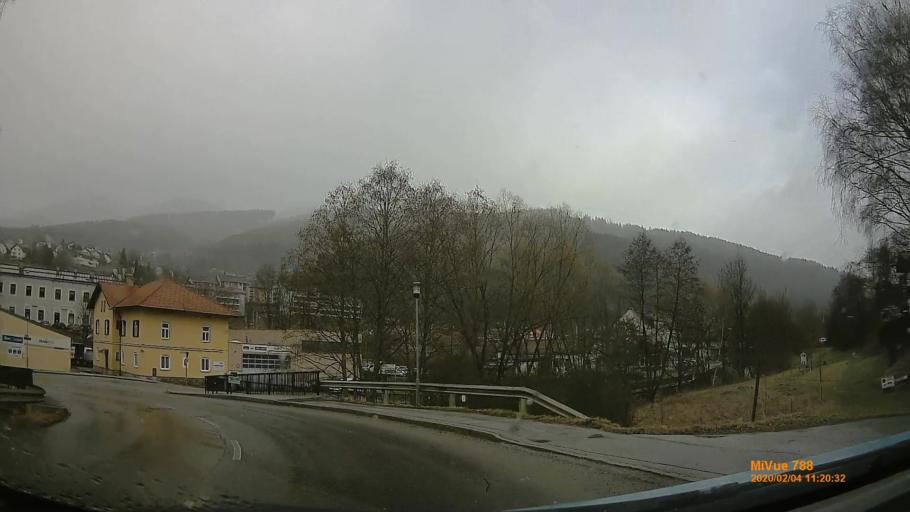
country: AT
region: Styria
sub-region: Politischer Bezirk Bruck-Muerzzuschlag
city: Muerzzuschlag
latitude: 47.6065
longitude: 15.6773
